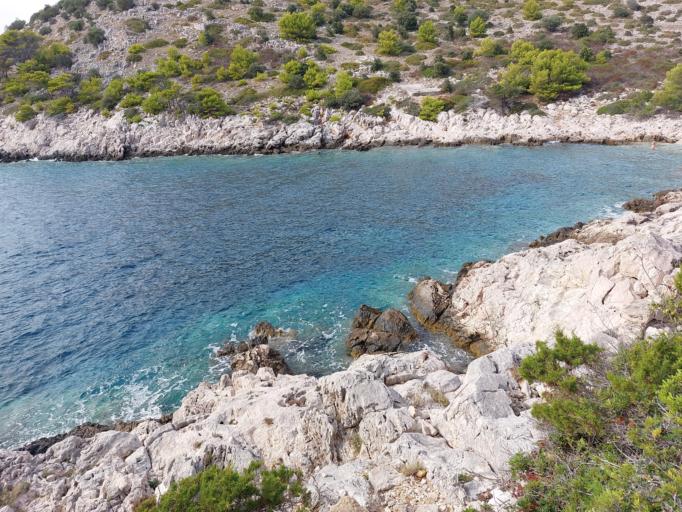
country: HR
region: Dubrovacko-Neretvanska
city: Smokvica
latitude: 42.7254
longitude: 16.8431
